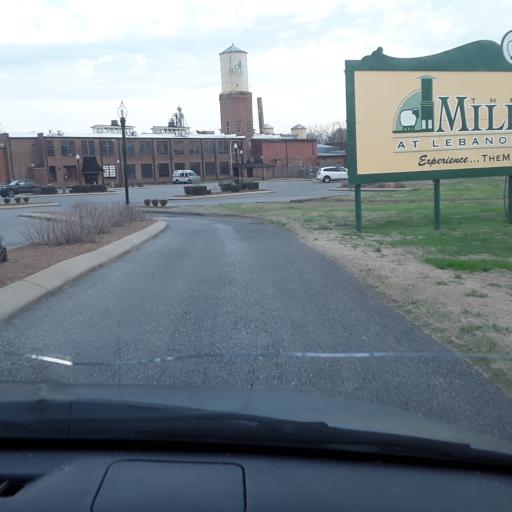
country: US
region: Tennessee
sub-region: Wilson County
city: Lebanon
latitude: 36.2120
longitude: -86.2949
